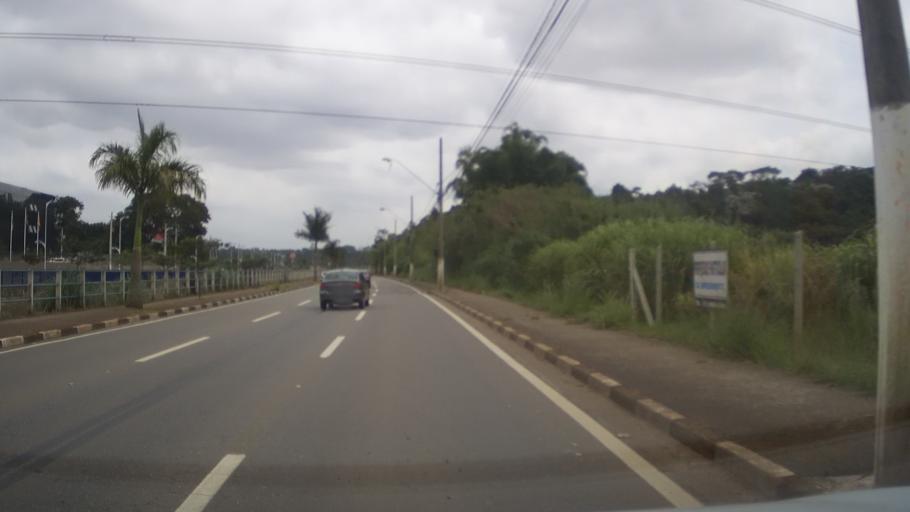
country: BR
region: Sao Paulo
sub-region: Aruja
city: Aruja
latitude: -23.4009
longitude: -46.3587
